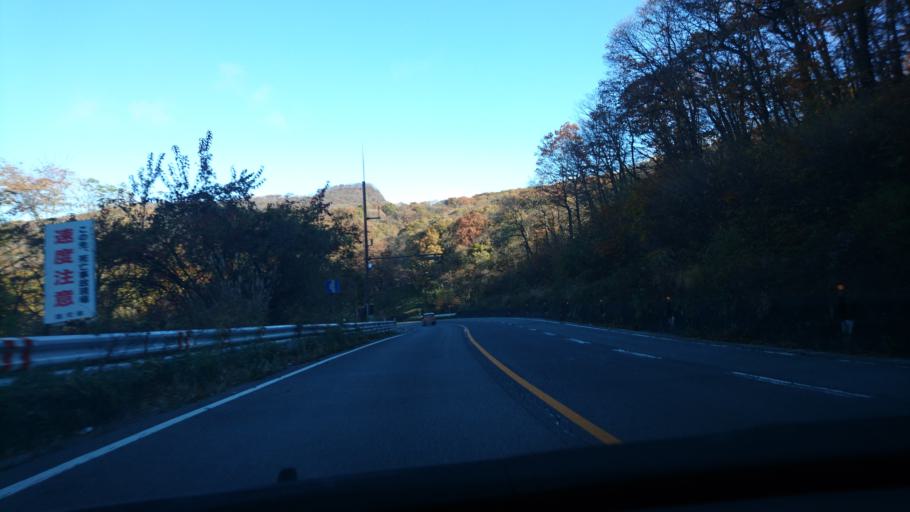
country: JP
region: Nagano
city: Saku
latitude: 36.3237
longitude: 138.6484
